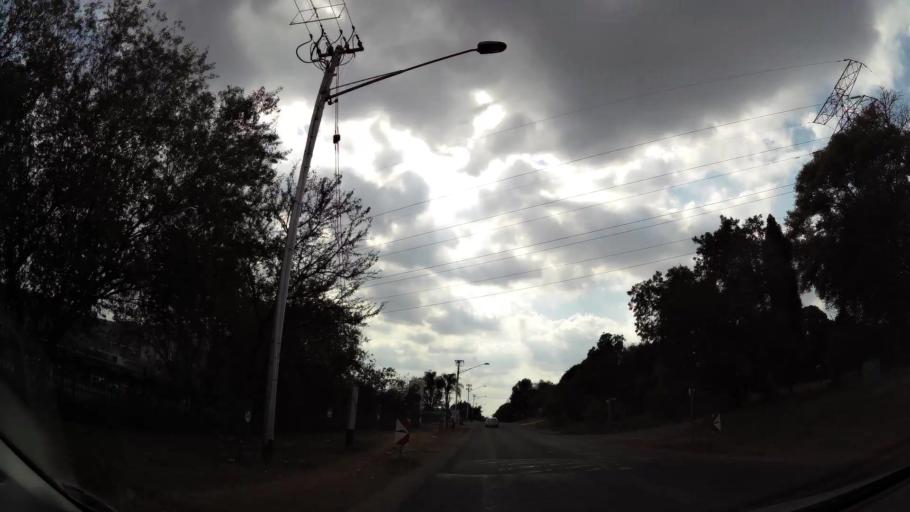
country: ZA
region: Gauteng
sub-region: City of Tshwane Metropolitan Municipality
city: Pretoria
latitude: -25.7669
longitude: 28.2884
